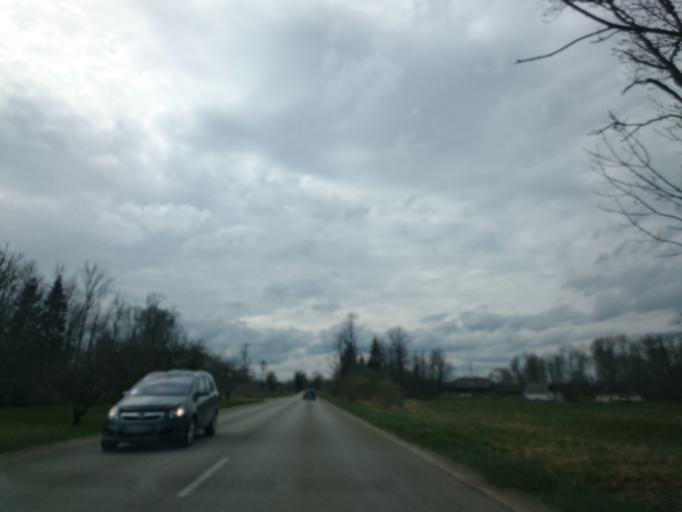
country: LV
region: Tukuma Rajons
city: Tukums
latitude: 56.9402
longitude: 23.1045
